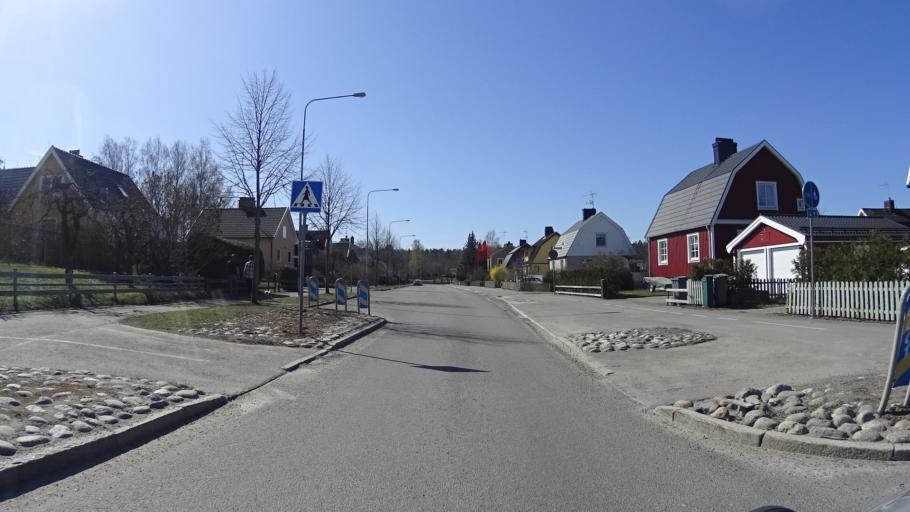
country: SE
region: Soedermanland
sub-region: Katrineholms Kommun
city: Katrineholm
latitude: 58.9904
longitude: 16.2286
